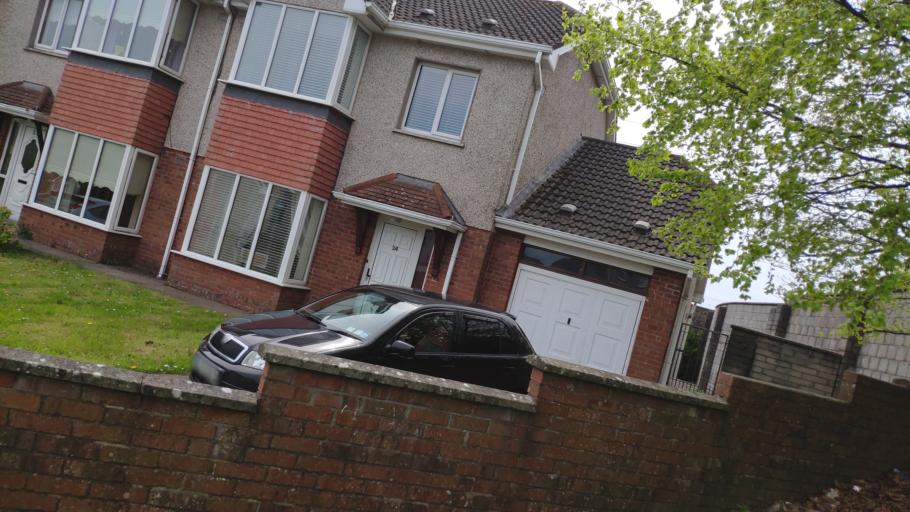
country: IE
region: Munster
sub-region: County Cork
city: Cork
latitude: 51.9237
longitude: -8.4587
